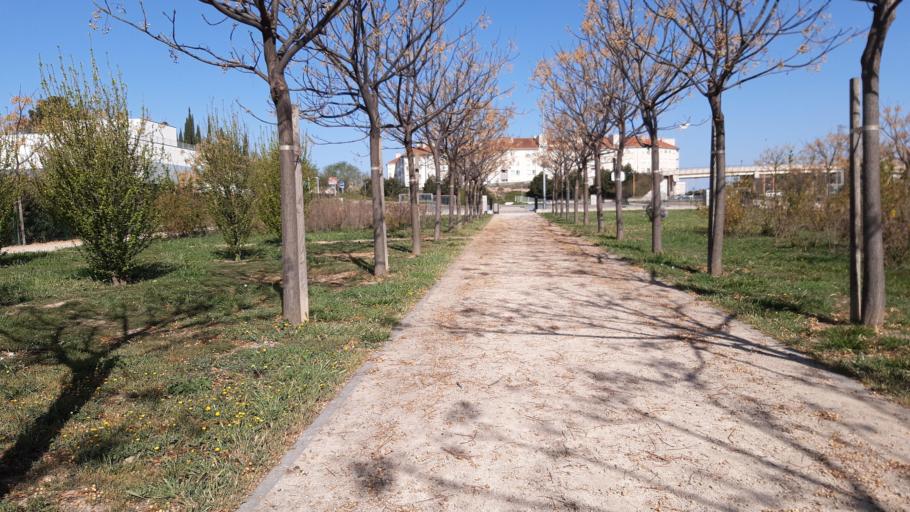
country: ES
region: Aragon
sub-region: Provincia de Zaragoza
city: Utebo
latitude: 41.7076
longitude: -0.9949
